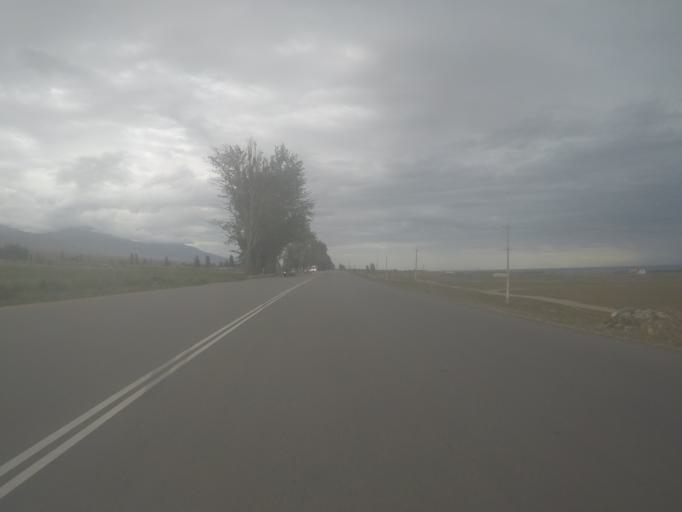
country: KG
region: Ysyk-Koel
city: Cholpon-Ata
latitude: 42.5936
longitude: 76.7573
